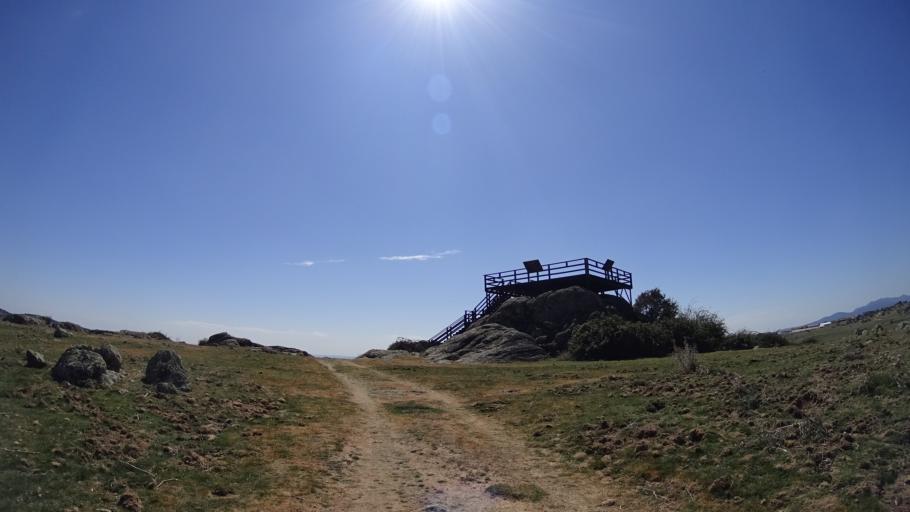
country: ES
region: Madrid
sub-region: Provincia de Madrid
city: Colmenar Viejo
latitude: 40.7061
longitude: -3.7497
